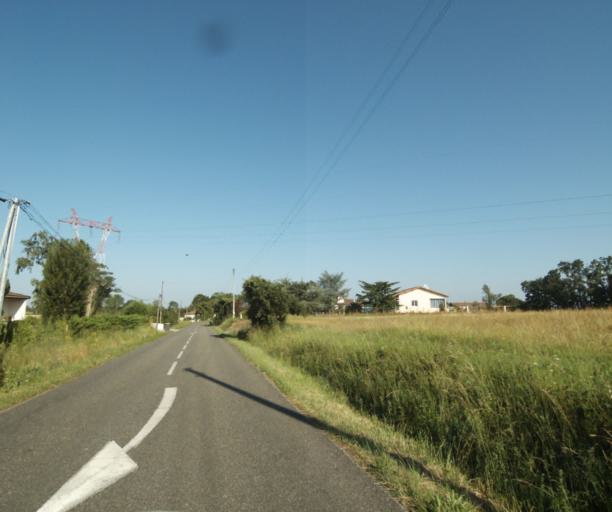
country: FR
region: Midi-Pyrenees
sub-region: Departement du Tarn-et-Garonne
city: Saint-Nauphary
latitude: 44.0157
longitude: 1.4240
